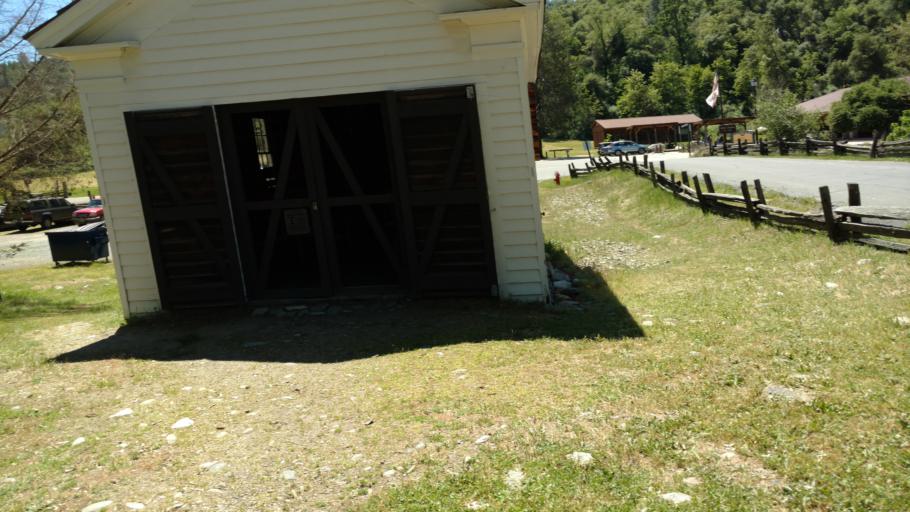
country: US
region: California
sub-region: El Dorado County
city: Placerville
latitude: 38.8006
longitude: -120.8914
